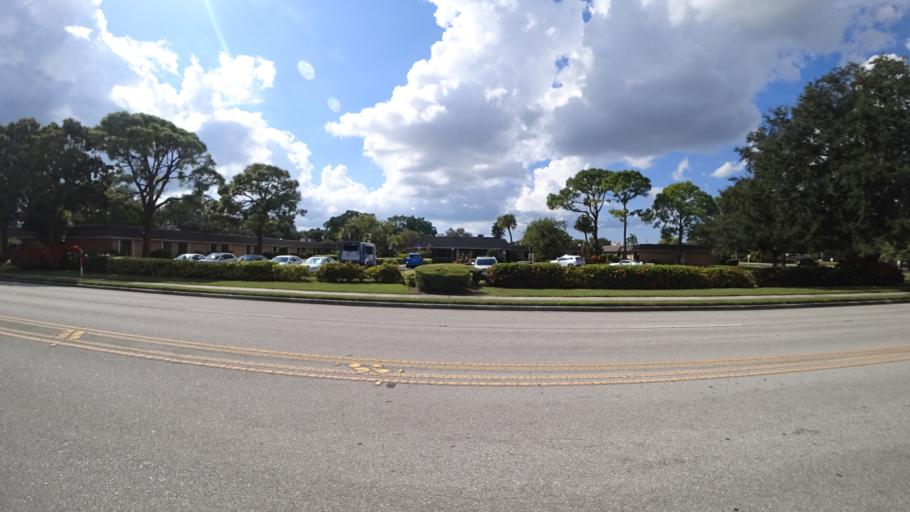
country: US
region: Florida
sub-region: Manatee County
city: Bayshore Gardens
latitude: 27.4418
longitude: -82.5876
